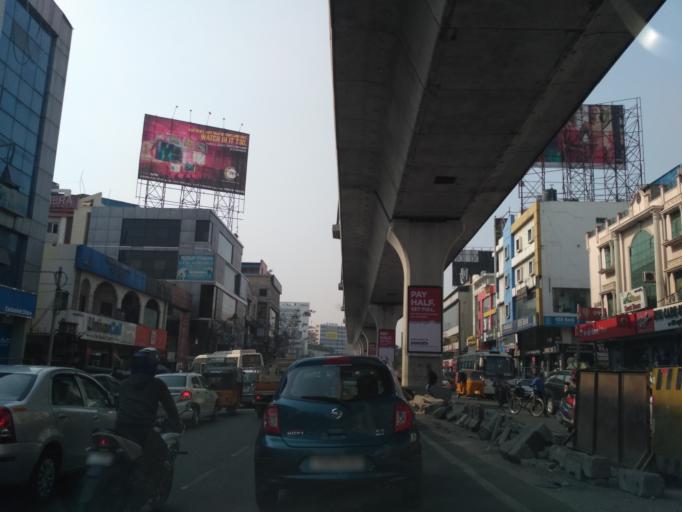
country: IN
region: Telangana
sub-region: Rangareddi
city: Kukatpalli
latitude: 17.4444
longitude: 78.3867
